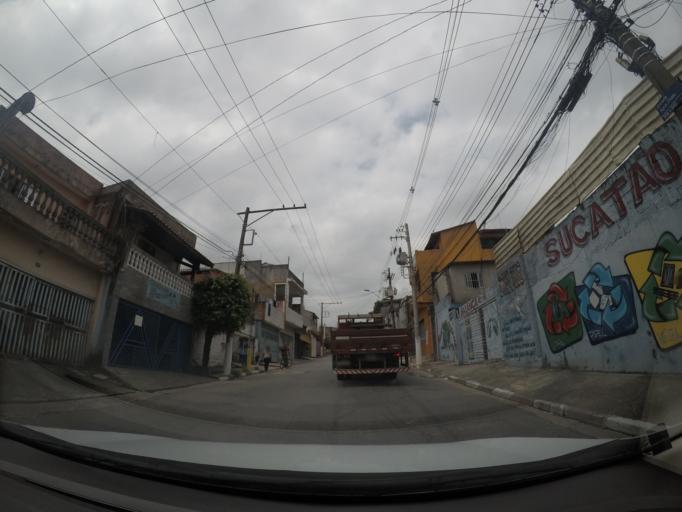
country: BR
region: Sao Paulo
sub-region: Itaquaquecetuba
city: Itaquaquecetuba
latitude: -23.4485
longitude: -46.4009
